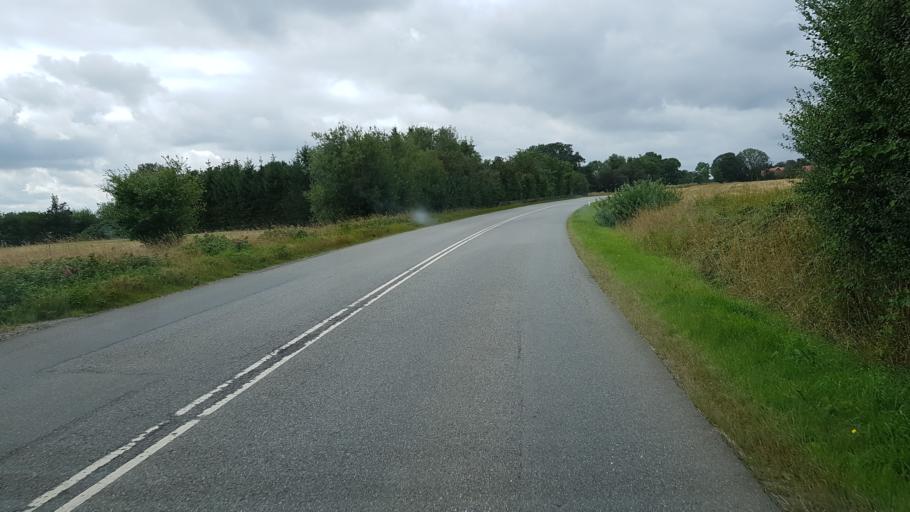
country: DK
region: South Denmark
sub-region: Kolding Kommune
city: Kolding
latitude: 55.4720
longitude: 9.4007
